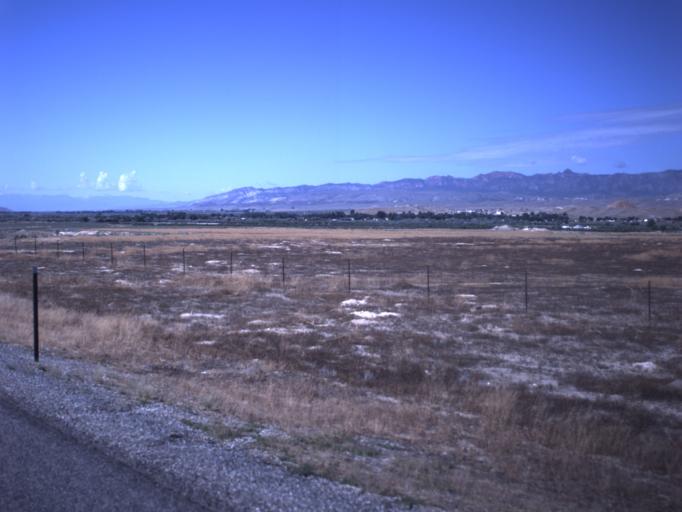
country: US
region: Utah
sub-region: Sevier County
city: Salina
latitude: 39.0218
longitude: -111.8326
